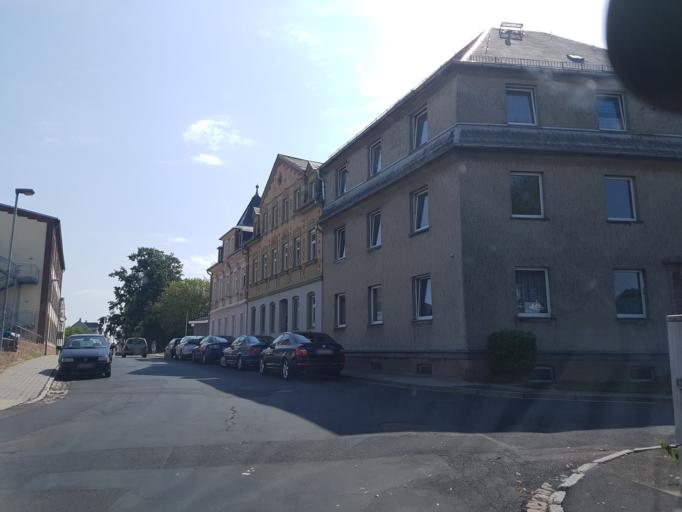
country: DE
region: Saxony
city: Waldheim
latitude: 51.0748
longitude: 13.0079
